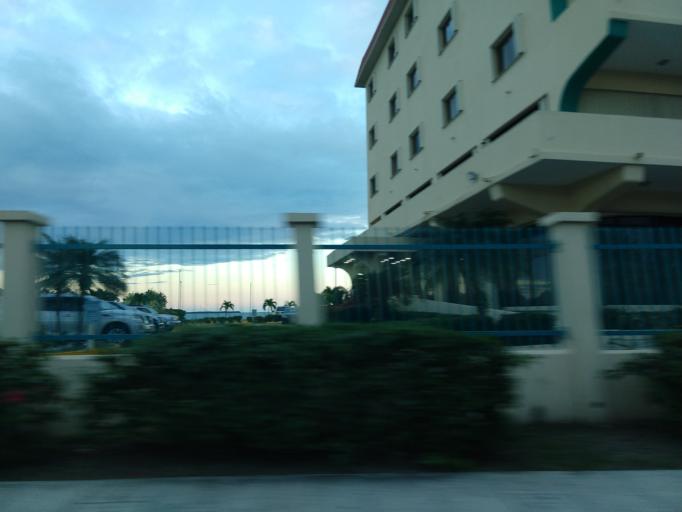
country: BZ
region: Belize
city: Belize City
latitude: 17.5088
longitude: -88.1876
